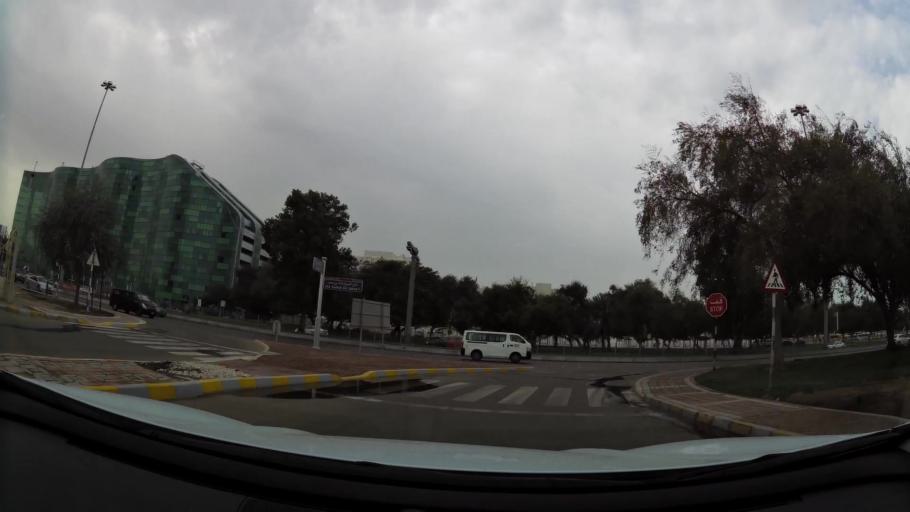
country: AE
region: Abu Dhabi
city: Abu Dhabi
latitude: 24.4231
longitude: 54.4564
